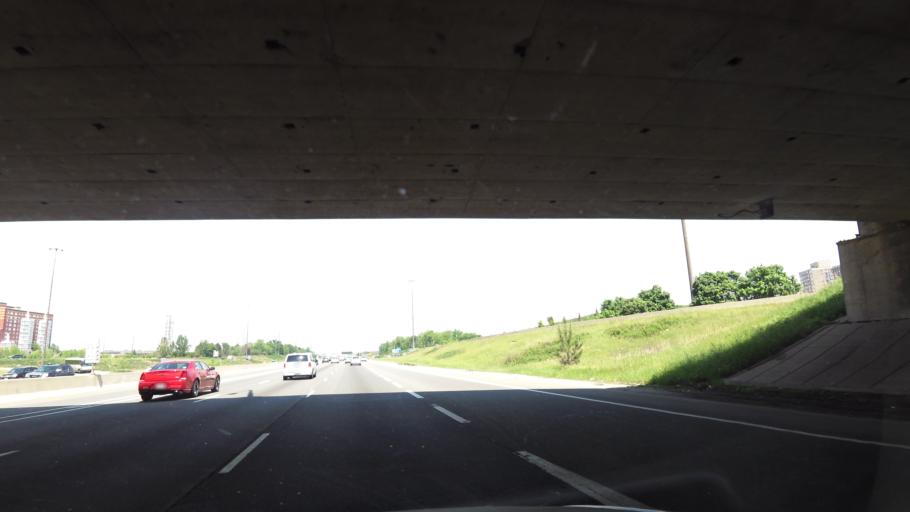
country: CA
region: Ontario
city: Mississauga
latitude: 43.6004
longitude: -79.6446
